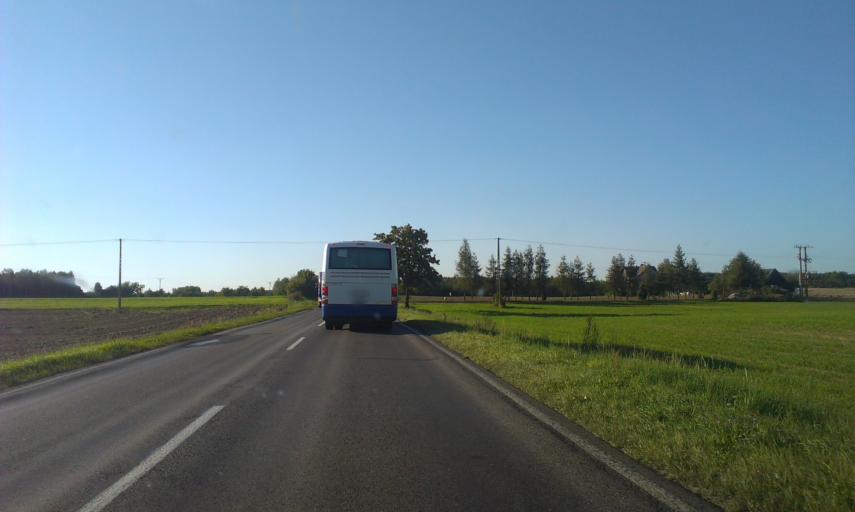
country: PL
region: Kujawsko-Pomorskie
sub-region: Powiat tucholski
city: Cekcyn
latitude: 53.5122
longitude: 17.9722
